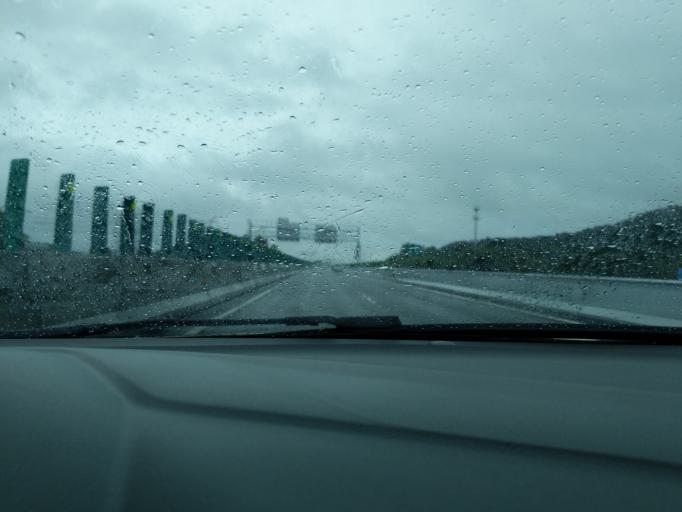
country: CN
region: Guangdong
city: Pingshi
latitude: 22.2548
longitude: 112.3098
